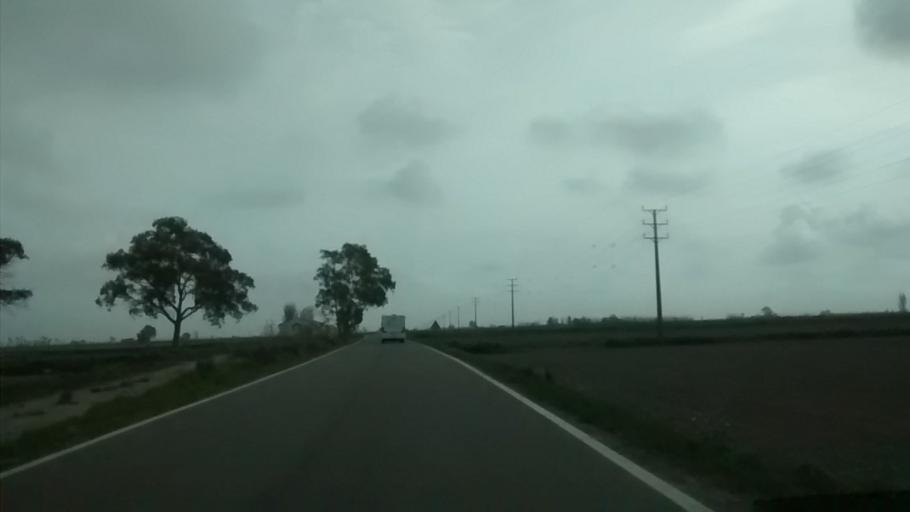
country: ES
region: Catalonia
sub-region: Provincia de Tarragona
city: Sant Carles de la Rapita
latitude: 40.6548
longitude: 0.6296
